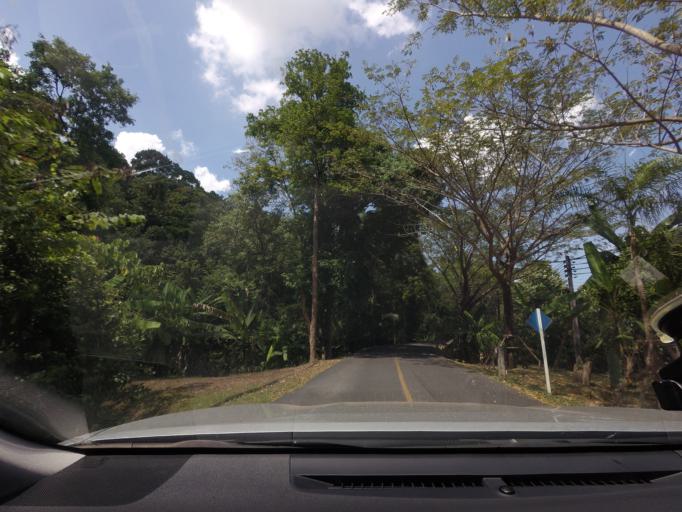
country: TH
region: Phuket
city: Mueang Phuket
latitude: 7.8738
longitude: 98.3528
